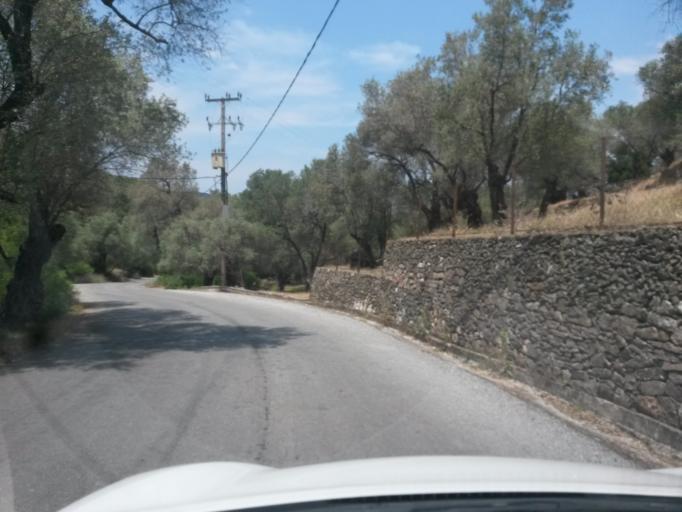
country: GR
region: North Aegean
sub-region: Nomos Lesvou
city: Pamfylla
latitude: 39.1735
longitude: 26.4821
